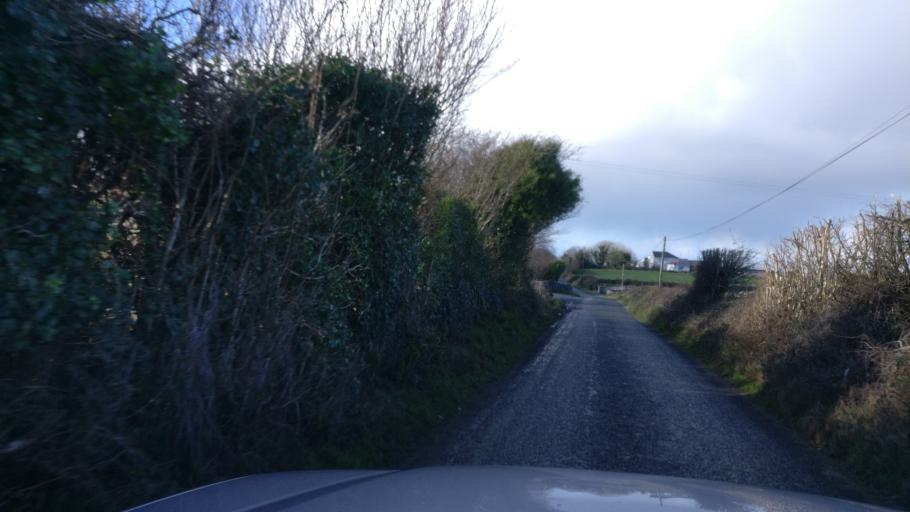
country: IE
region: Connaught
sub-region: County Galway
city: Athenry
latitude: 53.2384
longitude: -8.7987
